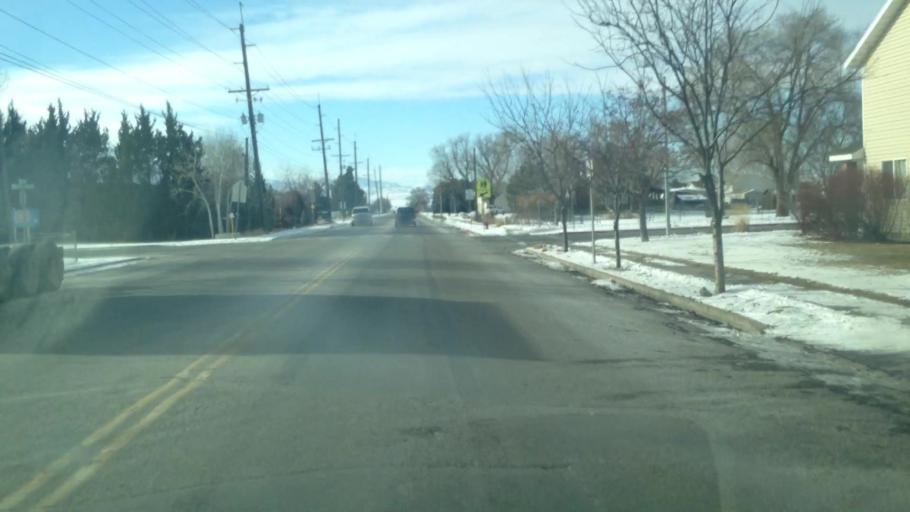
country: US
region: Utah
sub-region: Cache County
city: Logan
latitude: 41.7503
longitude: -111.8442
